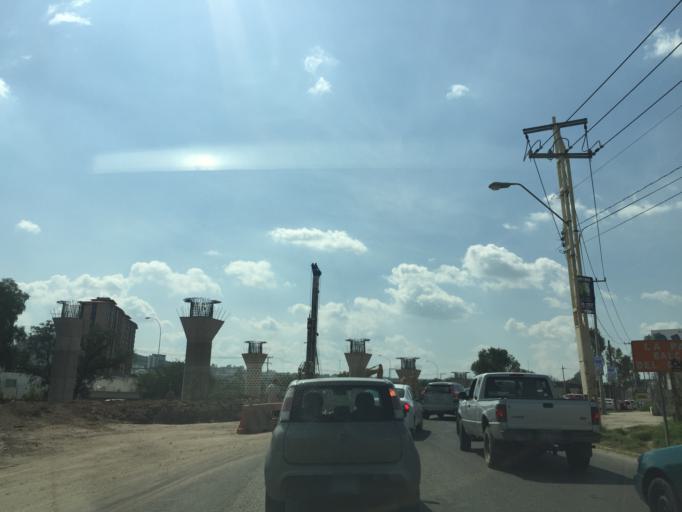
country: MX
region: Guanajuato
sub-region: Leon
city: La Ermita
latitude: 21.1688
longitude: -101.6948
